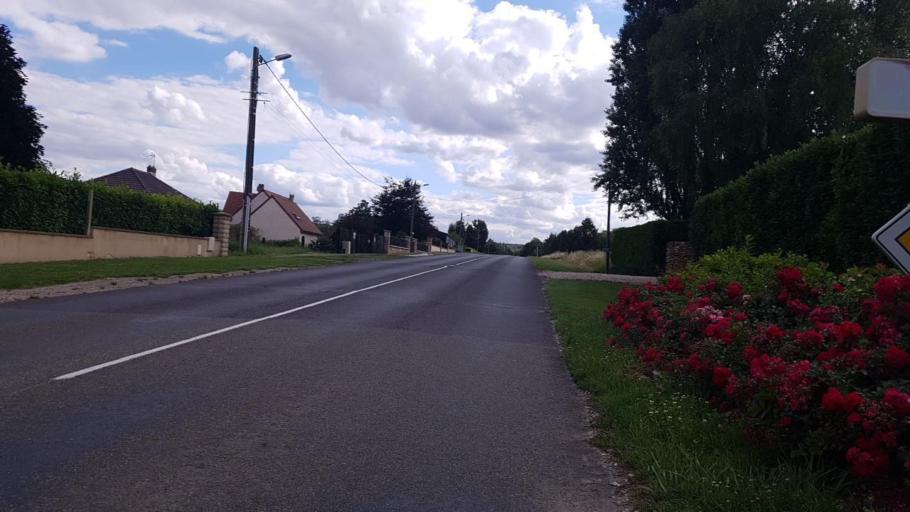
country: FR
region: Picardie
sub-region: Departement de l'Aisne
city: Crezancy
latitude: 49.0530
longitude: 3.4707
